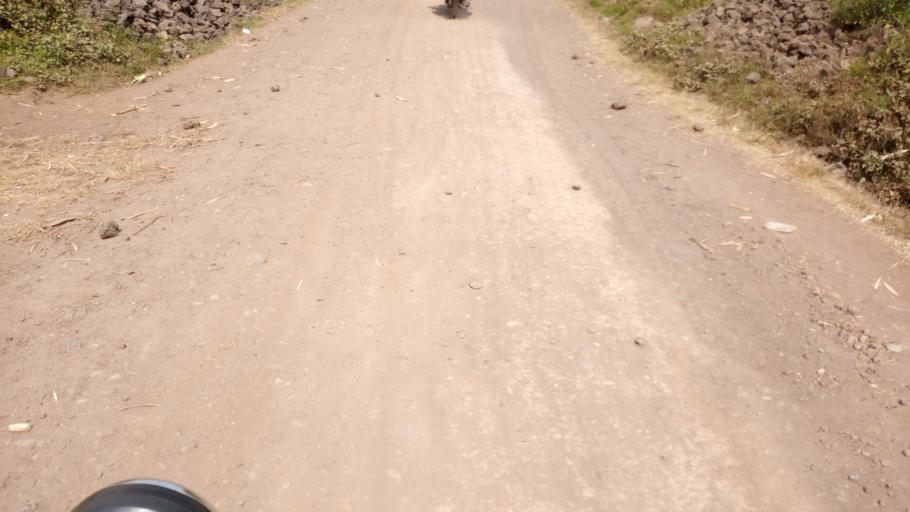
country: UG
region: Western Region
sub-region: Kisoro District
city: Kisoro
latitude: -1.3309
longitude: 29.7598
